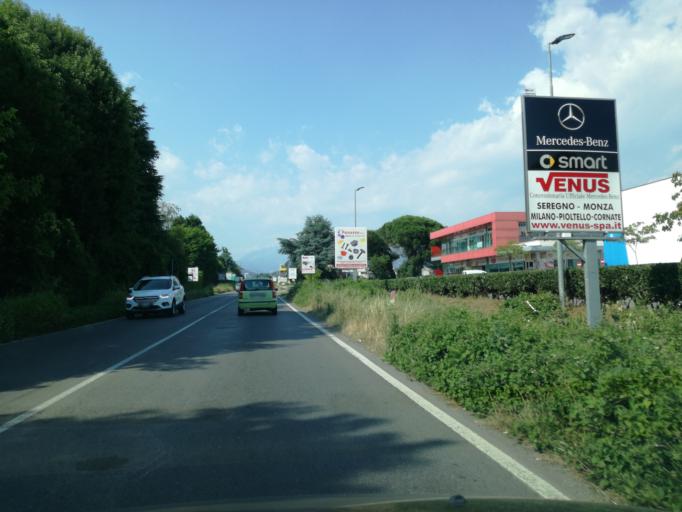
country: IT
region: Lombardy
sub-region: Provincia di Lecco
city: Osnago
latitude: 45.6805
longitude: 9.3974
